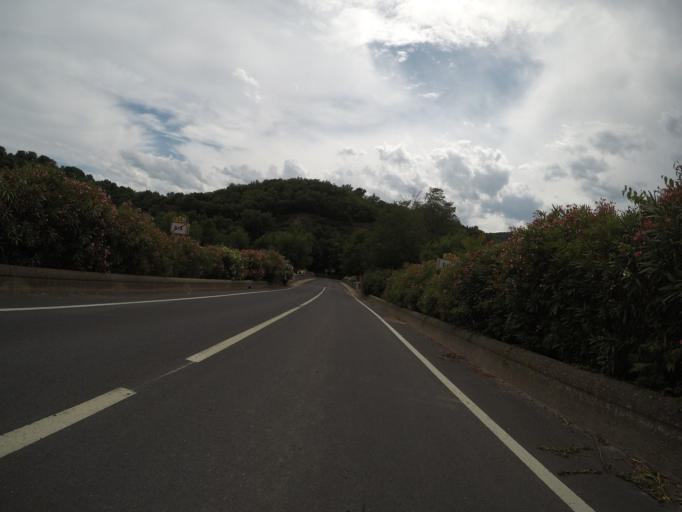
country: FR
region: Languedoc-Roussillon
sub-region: Departement des Pyrenees-Orientales
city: Ria-Sirach
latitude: 42.6094
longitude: 2.4038
